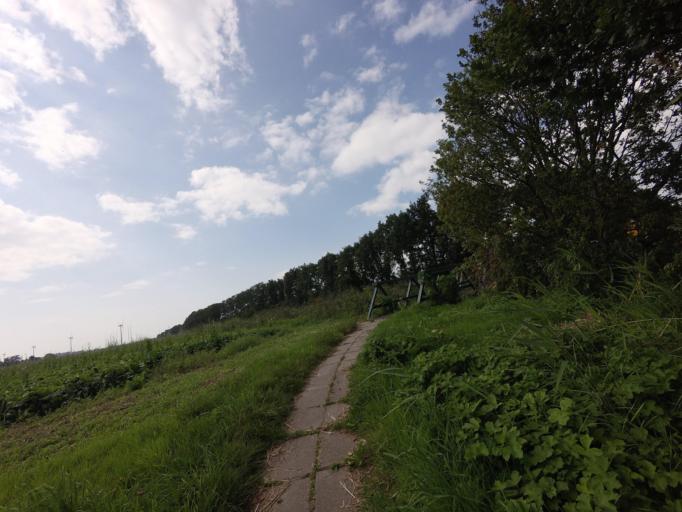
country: NL
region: Flevoland
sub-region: Gemeente Urk
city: Urk
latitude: 52.5740
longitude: 5.5826
